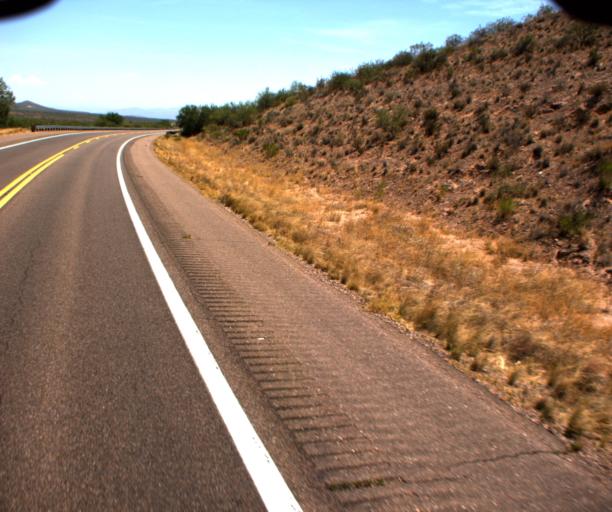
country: US
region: Arizona
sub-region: Gila County
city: Tonto Basin
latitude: 33.9179
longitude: -111.3158
